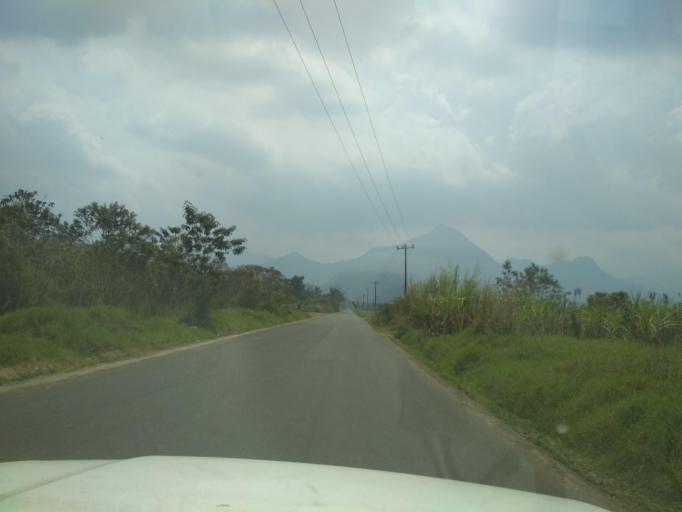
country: MX
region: Veracruz
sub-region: Cordoba
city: San Jose de Tapia
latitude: 18.8485
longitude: -96.9807
